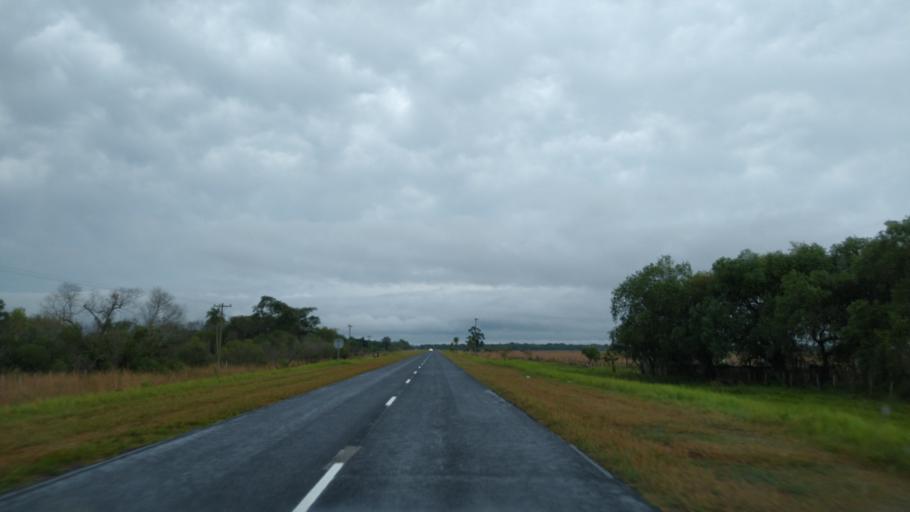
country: AR
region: Corrientes
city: Loreto
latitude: -27.7614
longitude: -57.2639
